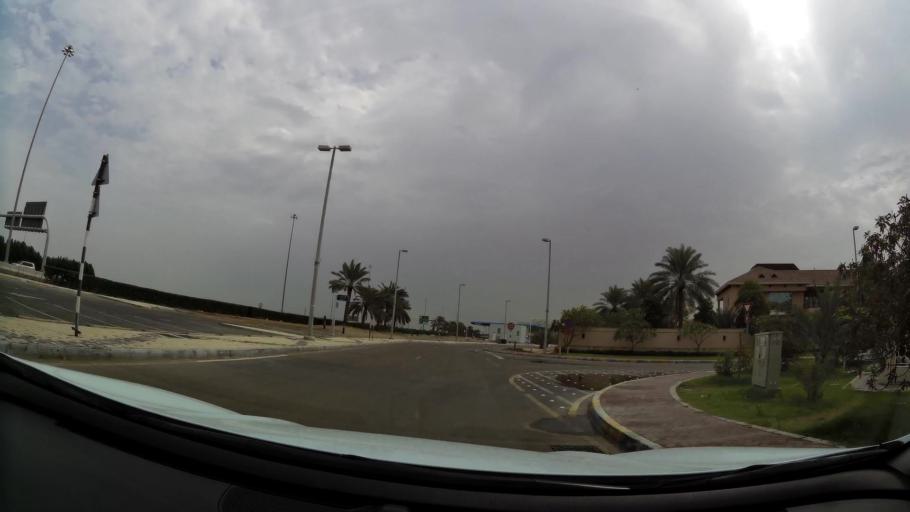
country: AE
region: Abu Dhabi
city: Abu Dhabi
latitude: 24.4410
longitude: 54.4500
